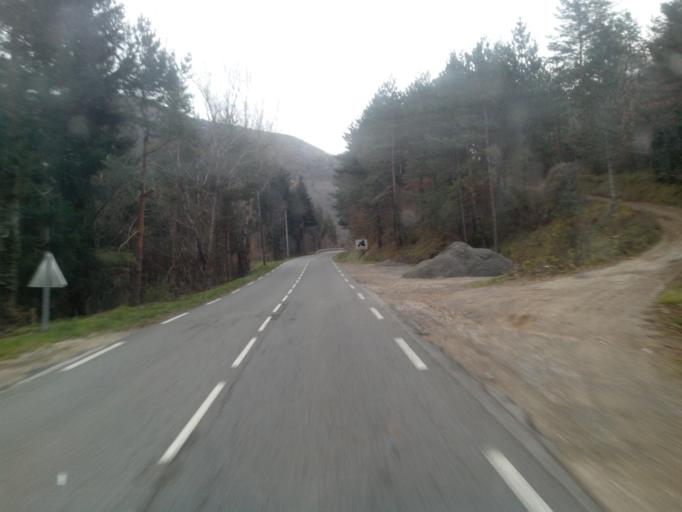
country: FR
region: Languedoc-Roussillon
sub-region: Departement de la Lozere
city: Florac
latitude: 44.3025
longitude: 3.5980
